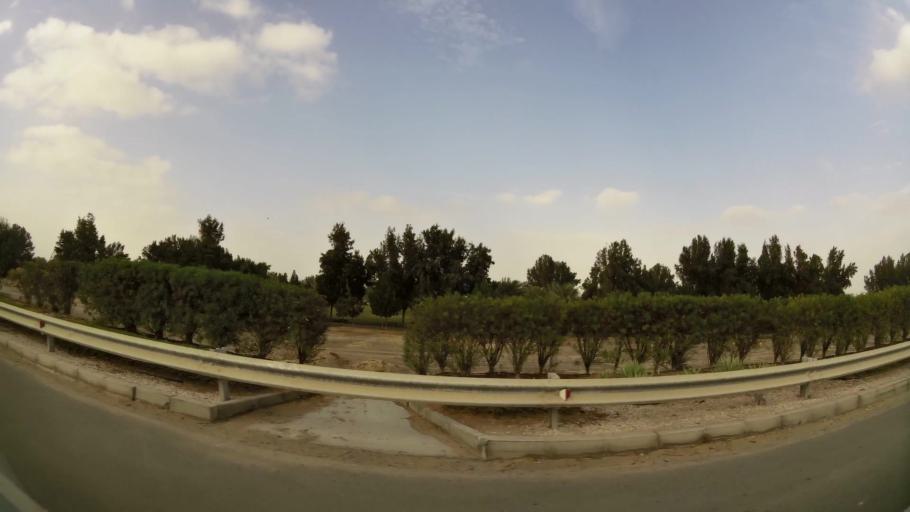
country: AE
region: Abu Dhabi
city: Abu Dhabi
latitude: 24.4918
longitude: 54.6223
